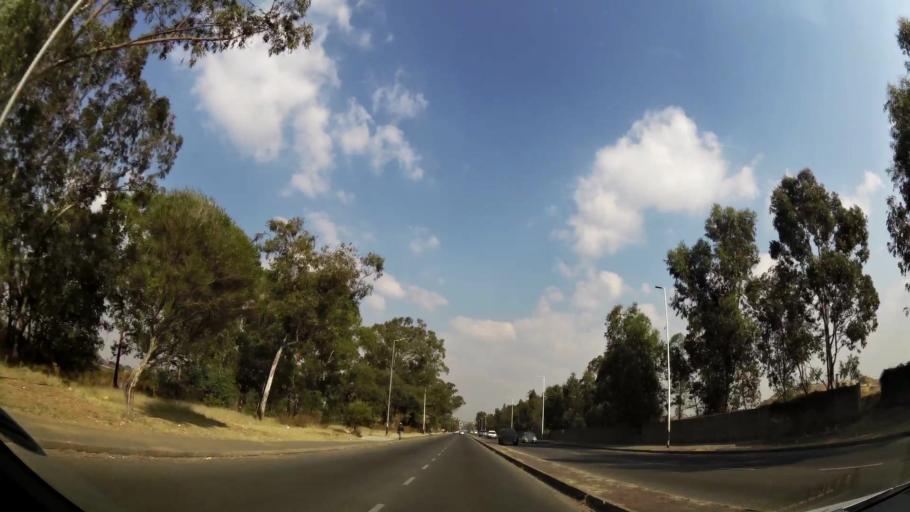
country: ZA
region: Gauteng
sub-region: Ekurhuleni Metropolitan Municipality
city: Boksburg
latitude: -26.2119
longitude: 28.2536
